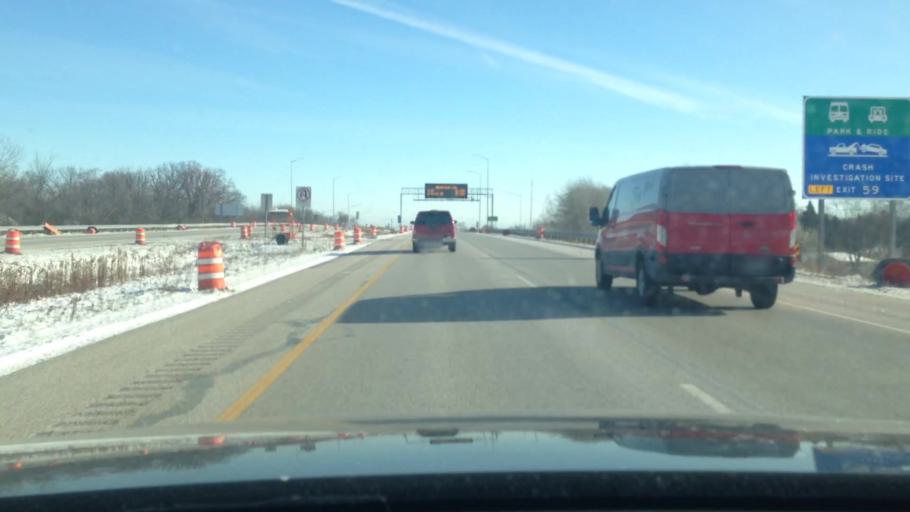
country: US
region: Wisconsin
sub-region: Waukesha County
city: New Berlin
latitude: 42.9586
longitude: -88.0826
